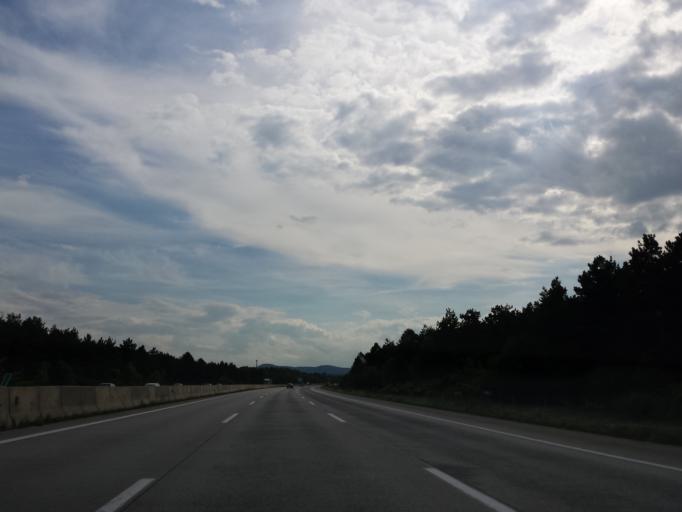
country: AT
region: Lower Austria
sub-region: Politischer Bezirk Wiener Neustadt
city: Bad Erlach
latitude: 47.7600
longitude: 16.2008
